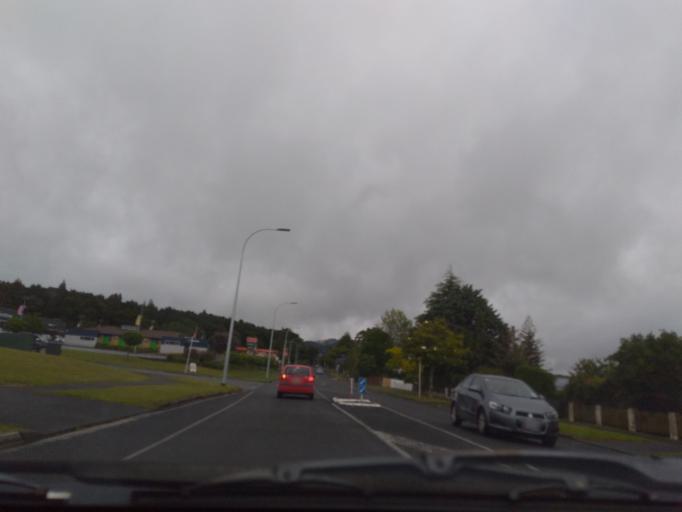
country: NZ
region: Northland
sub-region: Whangarei
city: Whangarei
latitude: -35.6835
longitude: 174.3233
